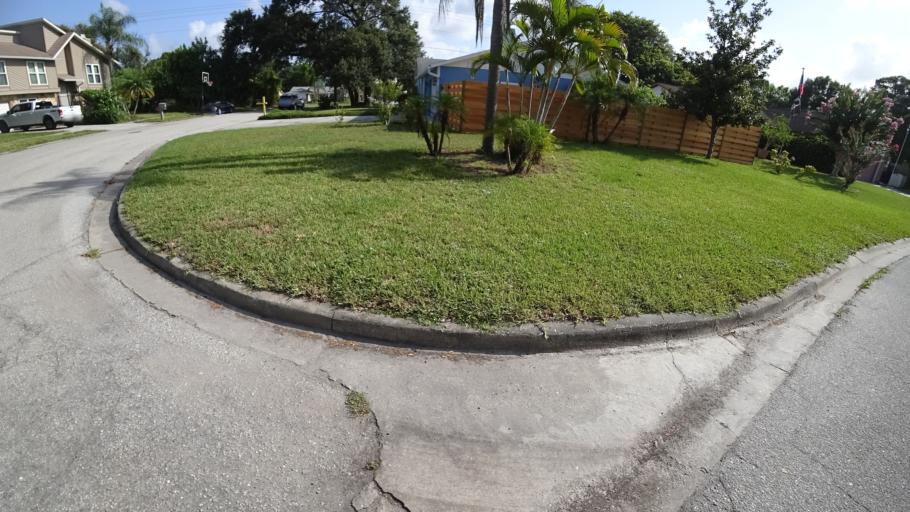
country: US
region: Florida
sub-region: Sarasota County
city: Desoto Lakes
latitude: 27.3956
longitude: -82.5020
